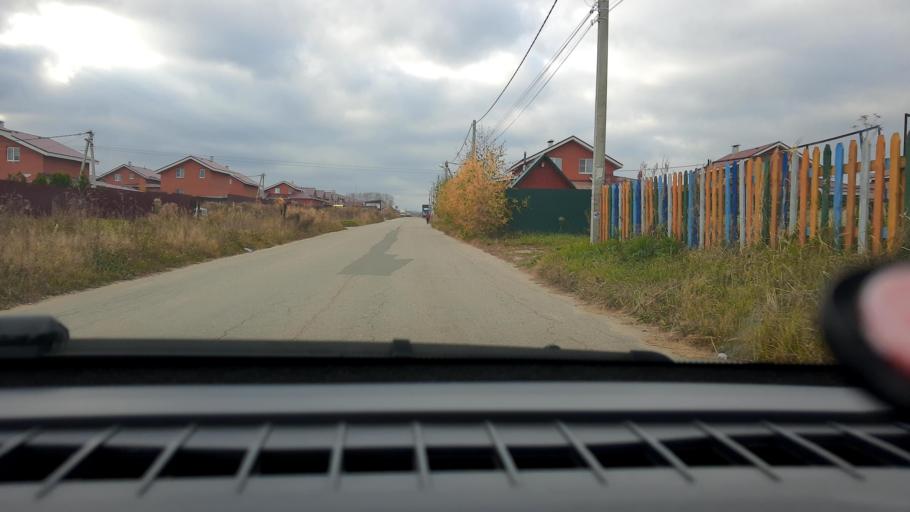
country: RU
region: Nizjnij Novgorod
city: Afonino
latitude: 56.1974
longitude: 44.0899
